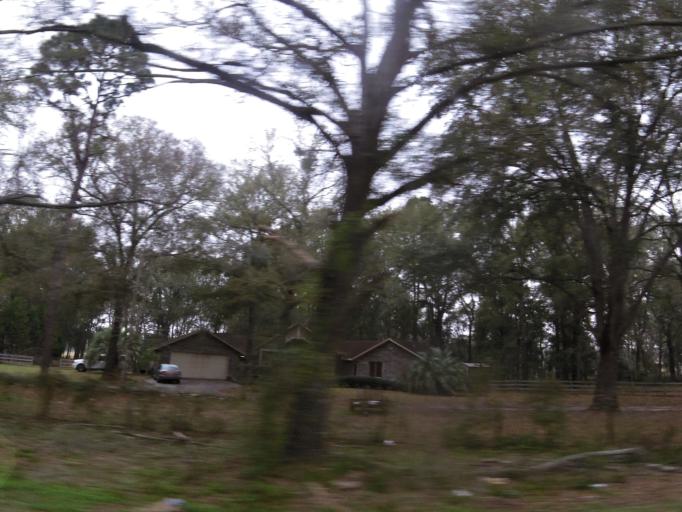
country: US
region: Florida
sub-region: Alachua County
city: High Springs
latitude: 29.8614
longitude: -82.5617
